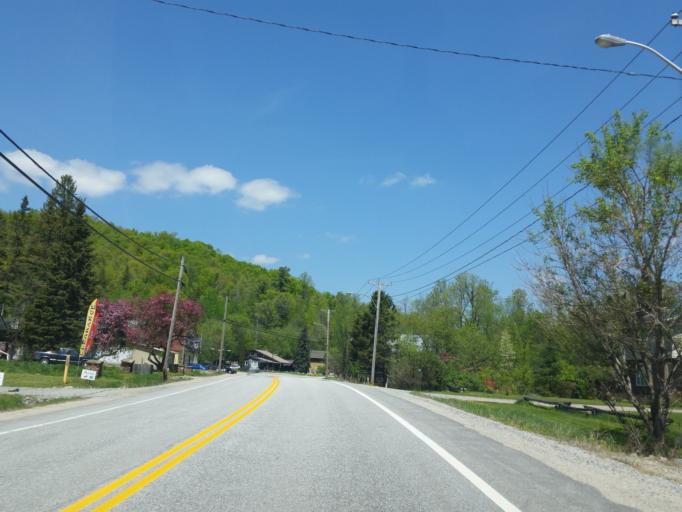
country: CA
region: Quebec
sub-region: Outaouais
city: Wakefield
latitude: 45.6814
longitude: -75.9307
